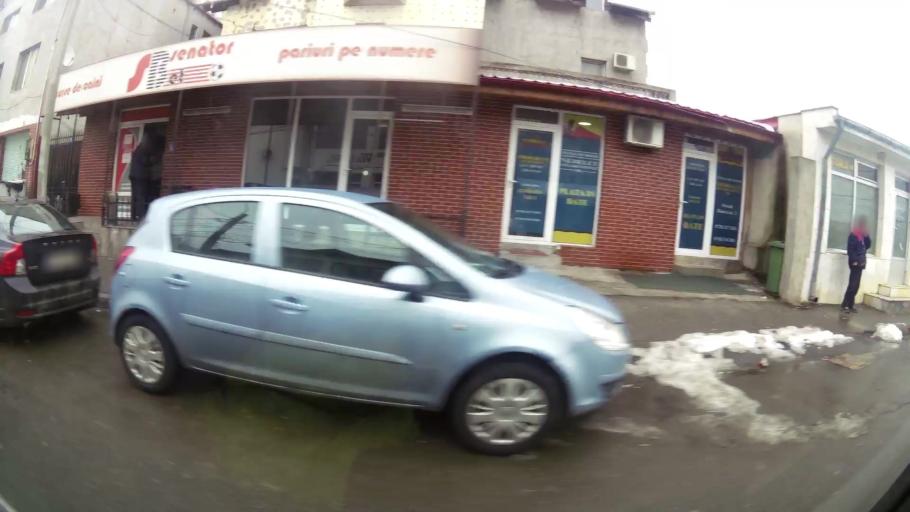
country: RO
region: Ilfov
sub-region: Comuna Popesti-Leordeni
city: Popesti-Leordeni
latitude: 44.4120
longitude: 26.1586
